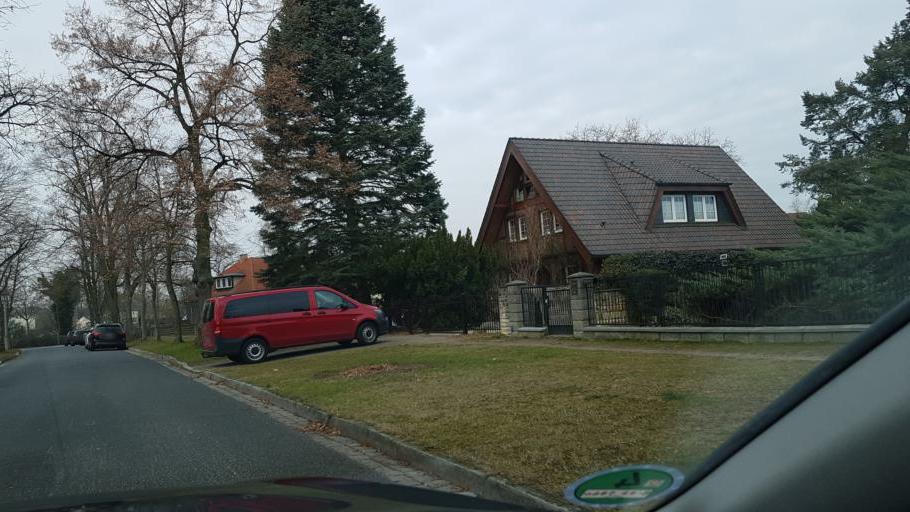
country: DE
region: Brandenburg
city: Konigs Wusterhausen
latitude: 52.2971
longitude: 13.6543
